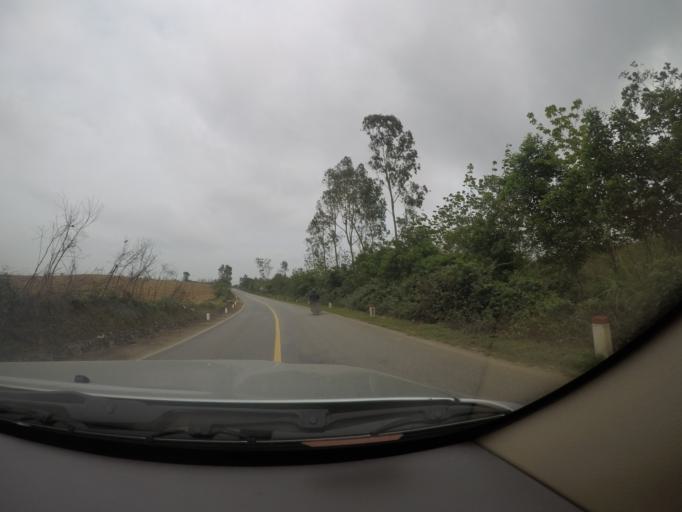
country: VN
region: Quang Binh
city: Hoan Lao
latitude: 17.4916
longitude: 106.5140
